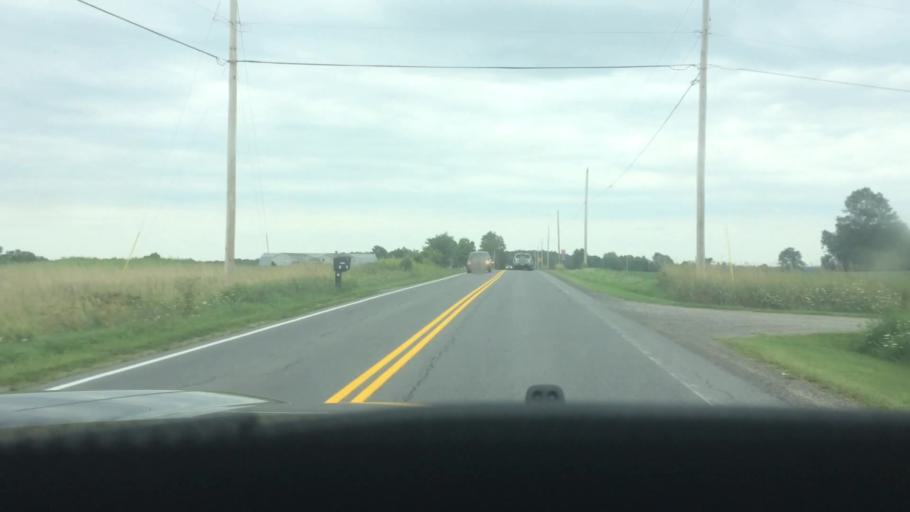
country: US
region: New York
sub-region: St. Lawrence County
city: Canton
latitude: 44.5514
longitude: -75.1405
